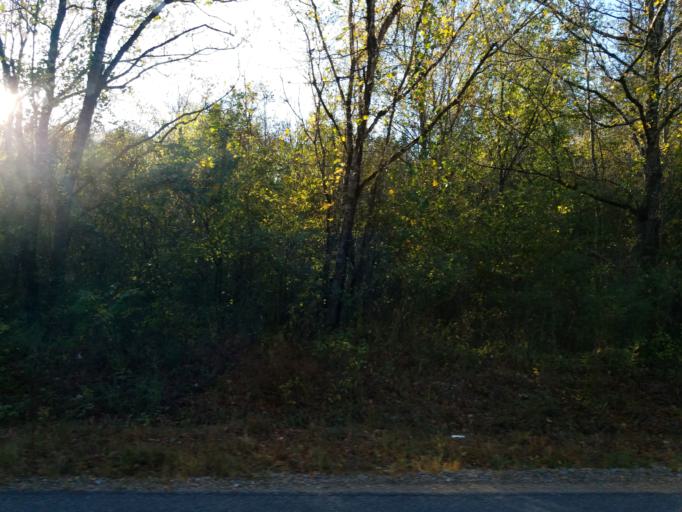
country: US
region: Georgia
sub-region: Bartow County
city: Euharlee
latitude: 34.2281
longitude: -84.9406
